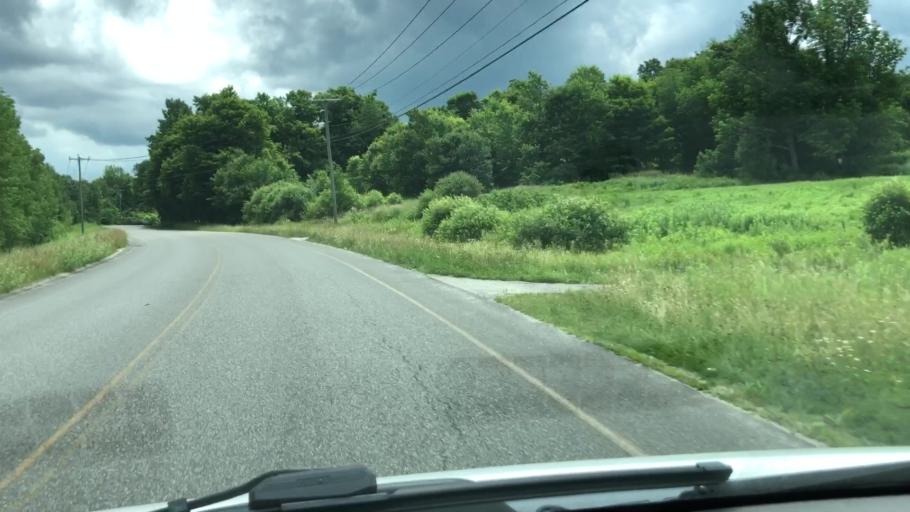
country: US
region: Massachusetts
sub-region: Berkshire County
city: Adams
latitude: 42.5439
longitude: -73.0532
